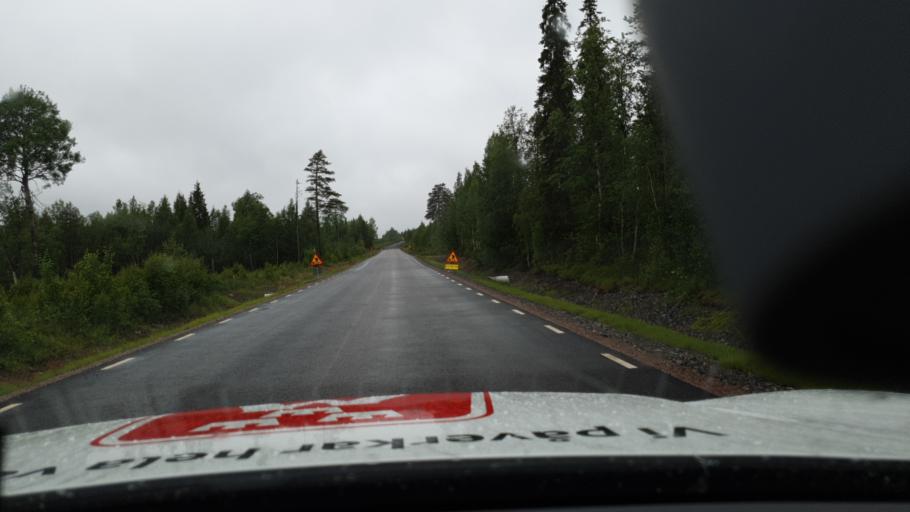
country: SE
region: Norrbotten
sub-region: Overtornea Kommun
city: OEvertornea
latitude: 66.5840
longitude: 23.3262
